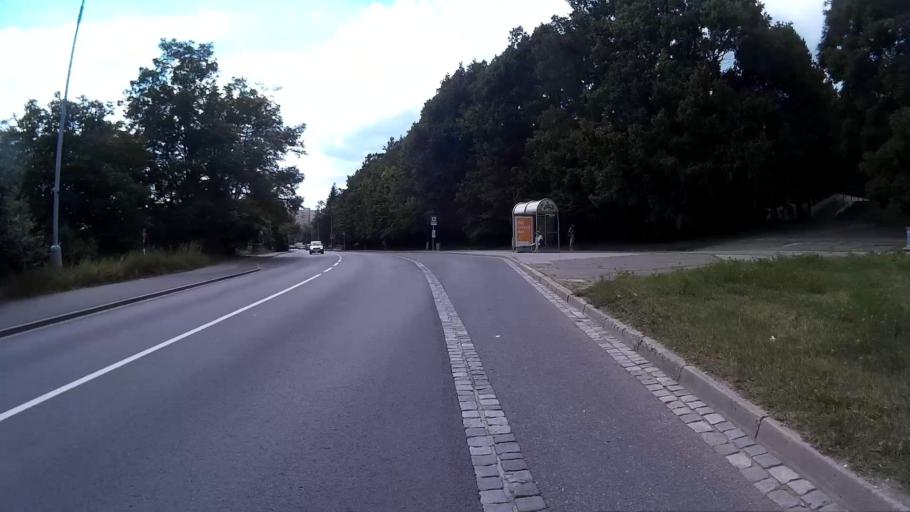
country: CZ
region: South Moravian
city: Moravany
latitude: 49.1661
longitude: 16.5858
